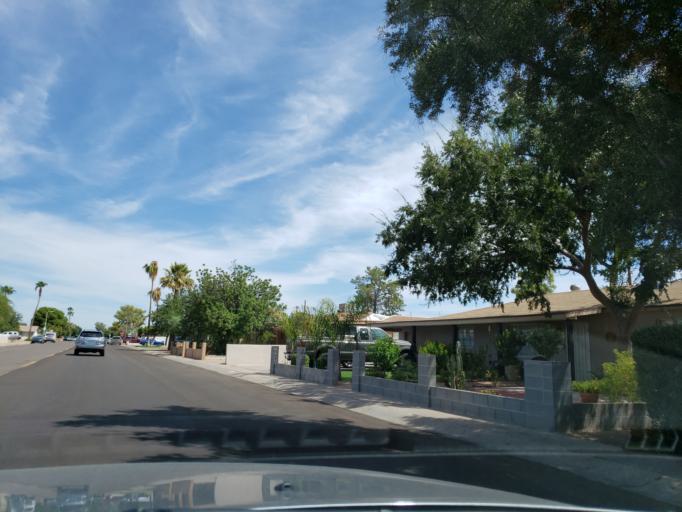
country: US
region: Arizona
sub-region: Maricopa County
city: Glendale
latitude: 33.5588
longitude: -112.1256
